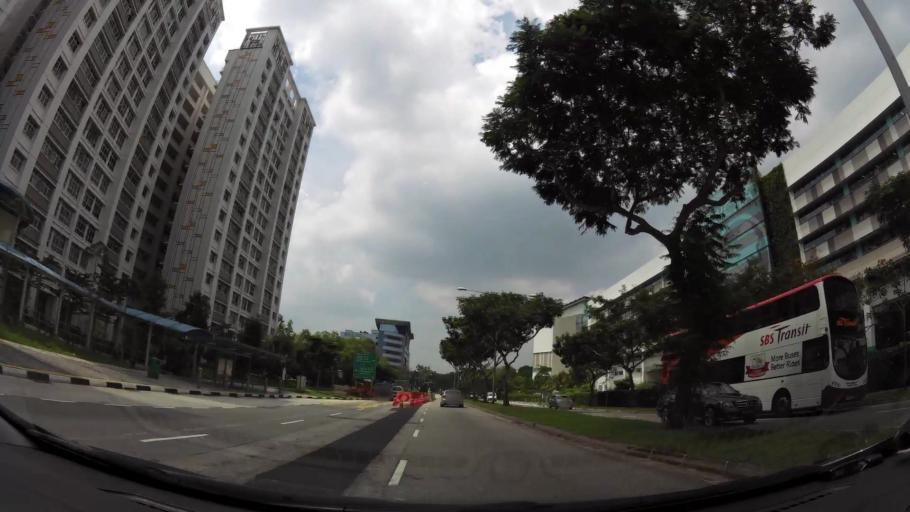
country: SG
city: Singapore
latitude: 1.3570
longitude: 103.9319
